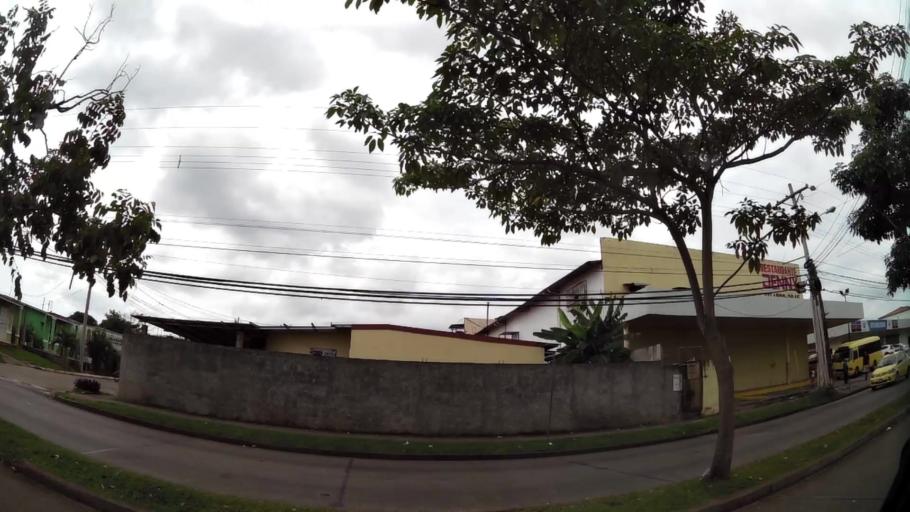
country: PA
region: Panama
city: San Miguelito
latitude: 9.0594
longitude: -79.4258
